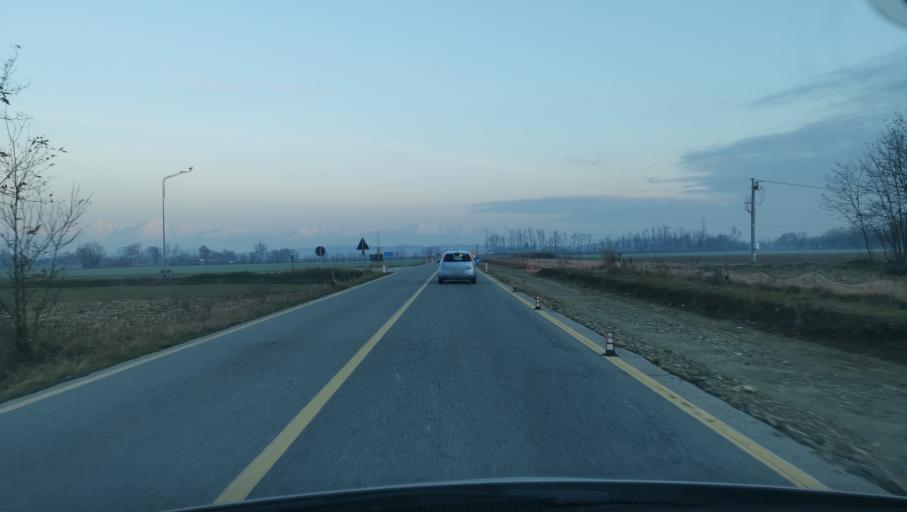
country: IT
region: Piedmont
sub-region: Provincia di Torino
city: Caluso
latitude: 45.2658
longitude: 7.8922
